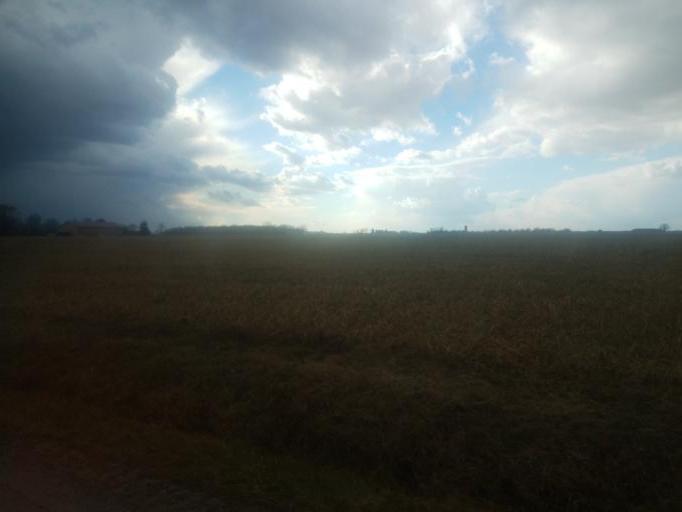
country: US
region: Ohio
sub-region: Marion County
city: Prospect
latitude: 40.4555
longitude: -83.1122
